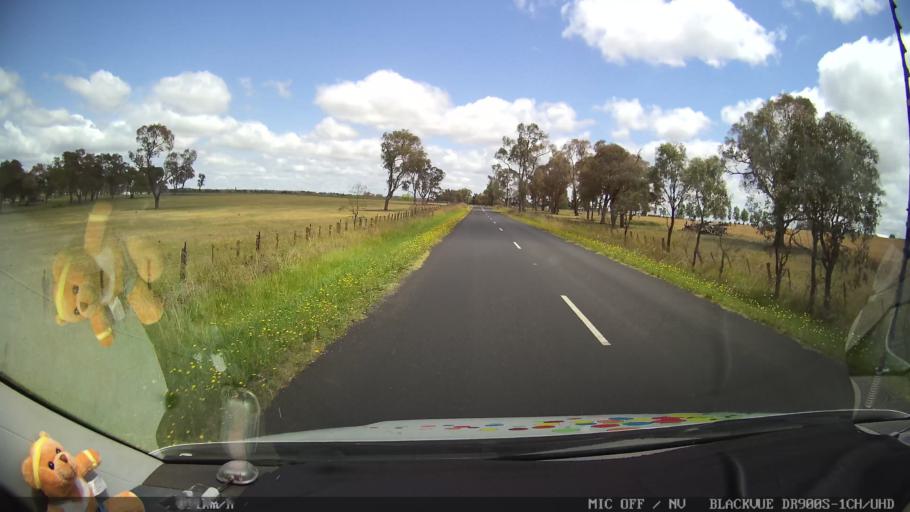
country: AU
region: New South Wales
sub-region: Glen Innes Severn
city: Glen Innes
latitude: -29.6495
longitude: 151.6928
